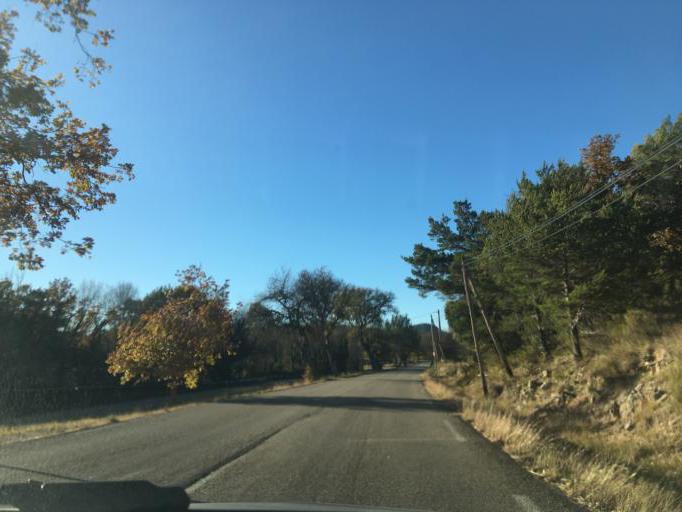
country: FR
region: Provence-Alpes-Cote d'Azur
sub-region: Departement du Var
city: Flayosc
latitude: 43.6030
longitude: 6.3623
